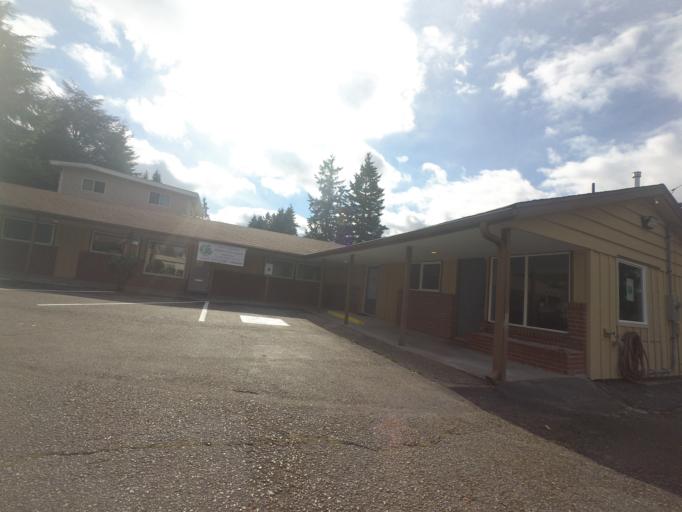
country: US
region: Washington
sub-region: Pierce County
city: University Place
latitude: 47.2350
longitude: -122.5457
